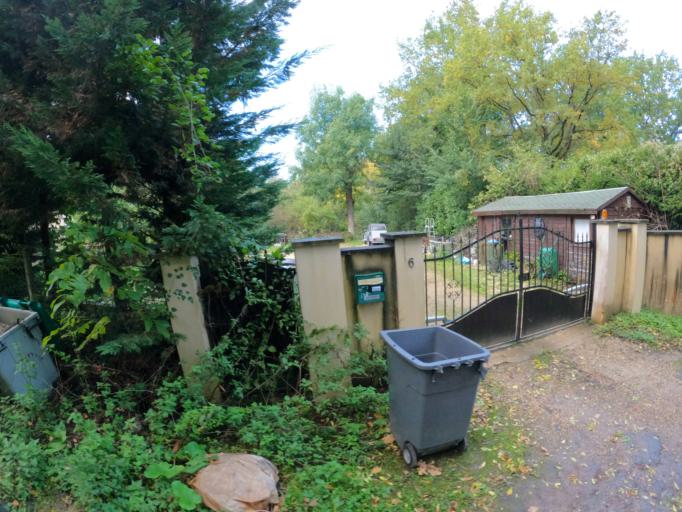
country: FR
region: Ile-de-France
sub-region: Departement de Seine-et-Marne
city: Saint-Germain-sur-Morin
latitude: 48.8749
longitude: 2.8541
